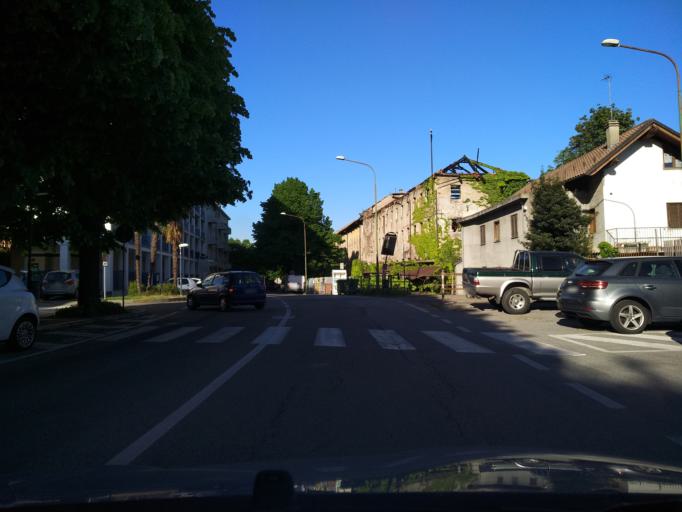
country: IT
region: Piedmont
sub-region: Provincia di Torino
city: Pinerolo
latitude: 44.8822
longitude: 7.3339
